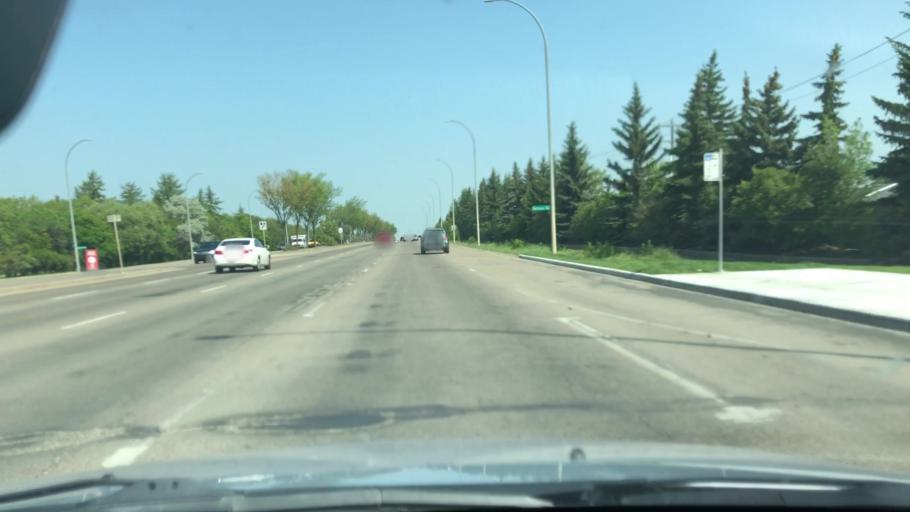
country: CA
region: Alberta
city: Edmonton
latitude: 53.6076
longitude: -113.4917
